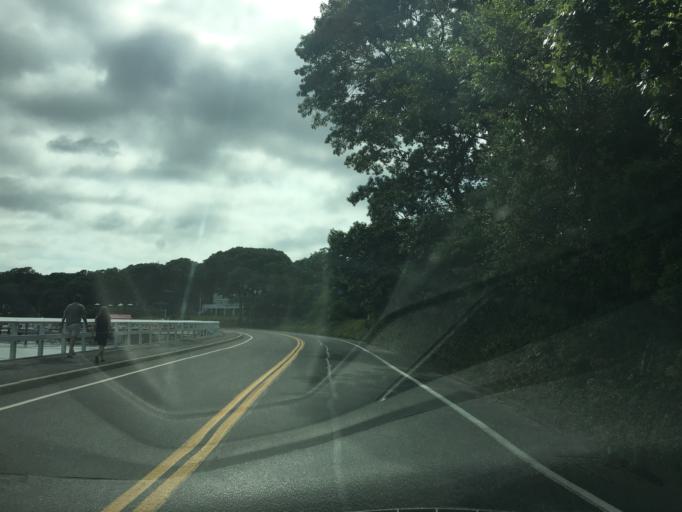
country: US
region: New York
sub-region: Suffolk County
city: Shelter Island Heights
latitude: 41.0701
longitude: -72.3775
